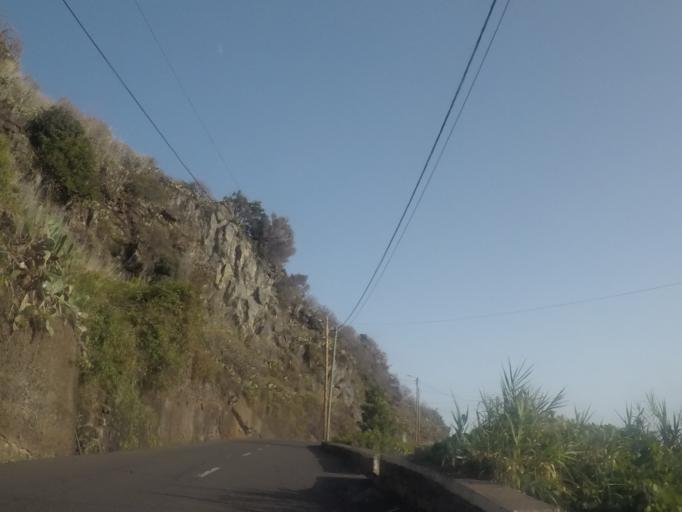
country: PT
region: Madeira
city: Ribeira Brava
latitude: 32.6786
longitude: -17.0715
